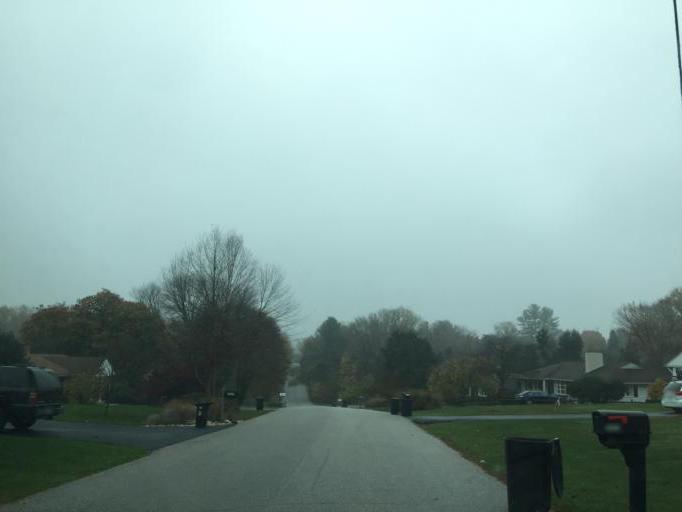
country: US
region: Maryland
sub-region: Howard County
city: Riverside
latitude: 39.1935
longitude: -76.8630
